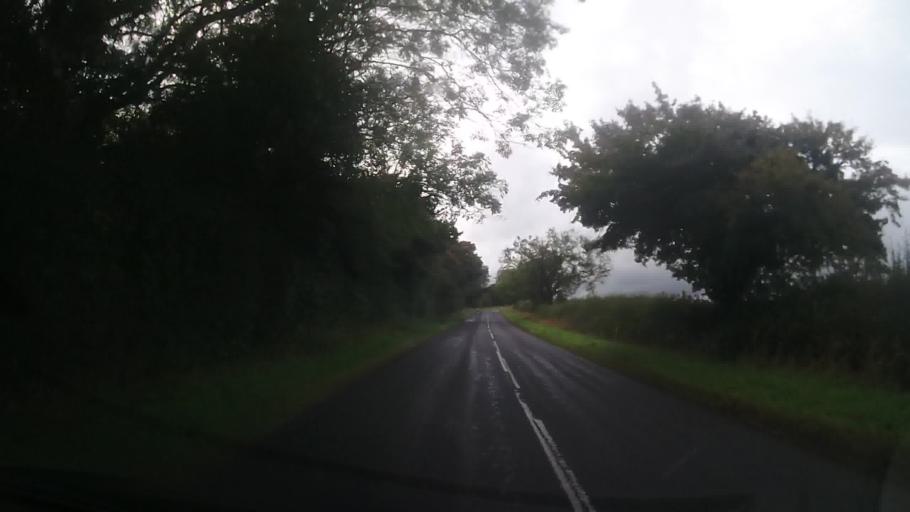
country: GB
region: England
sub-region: Oxfordshire
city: Chipping Norton
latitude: 51.9256
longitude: -1.5169
